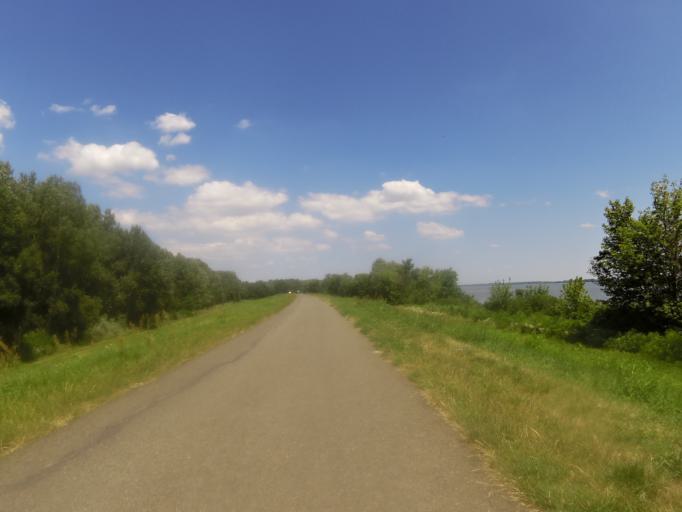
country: HU
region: Heves
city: Tiszanana
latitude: 47.5571
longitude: 20.6058
